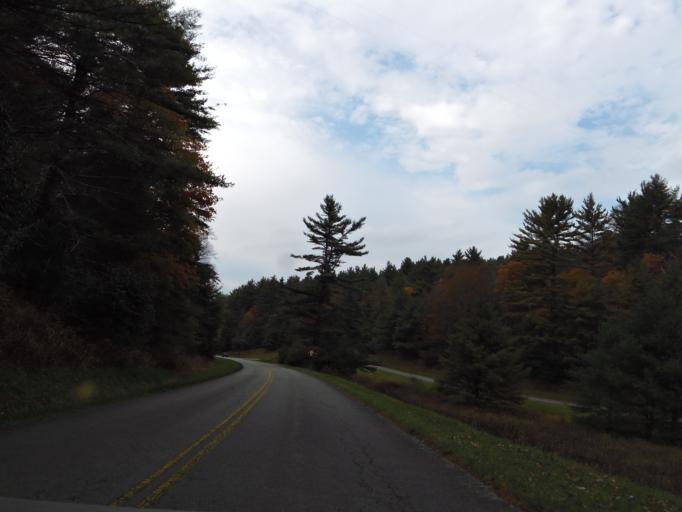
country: US
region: North Carolina
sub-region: Alleghany County
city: Sparta
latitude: 36.3924
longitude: -81.2075
